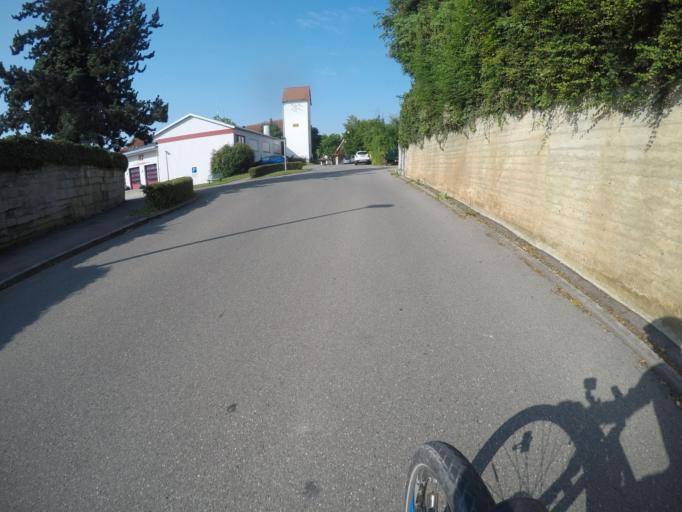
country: DE
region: Baden-Wuerttemberg
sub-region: Regierungsbezirk Stuttgart
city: Bondorf
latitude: 48.5222
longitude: 8.8316
